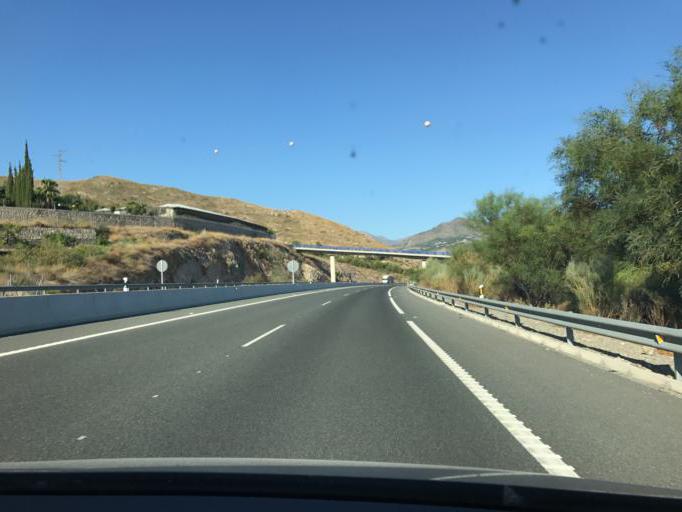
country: ES
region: Andalusia
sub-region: Provincia de Granada
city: Salobrena
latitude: 36.7760
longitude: -3.5666
